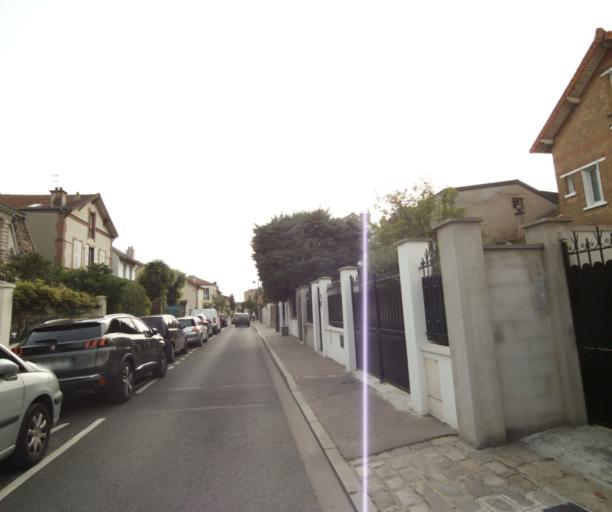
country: FR
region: Ile-de-France
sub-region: Departement des Hauts-de-Seine
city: Colombes
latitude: 48.9177
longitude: 2.2461
